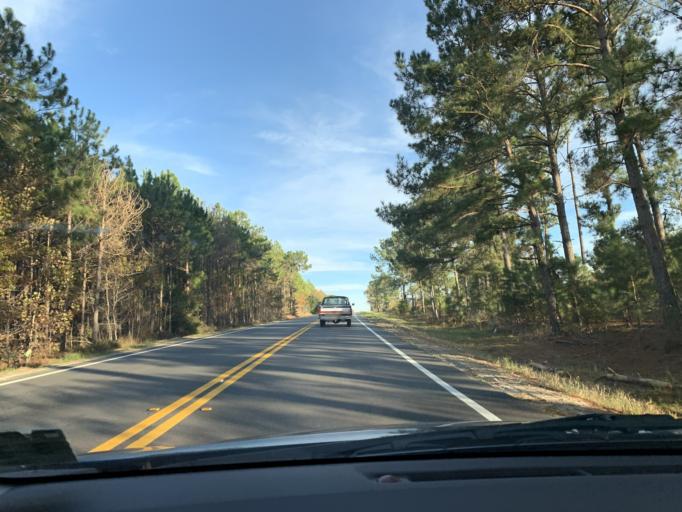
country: US
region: Georgia
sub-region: Irwin County
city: Ocilla
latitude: 31.5946
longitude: -83.1112
